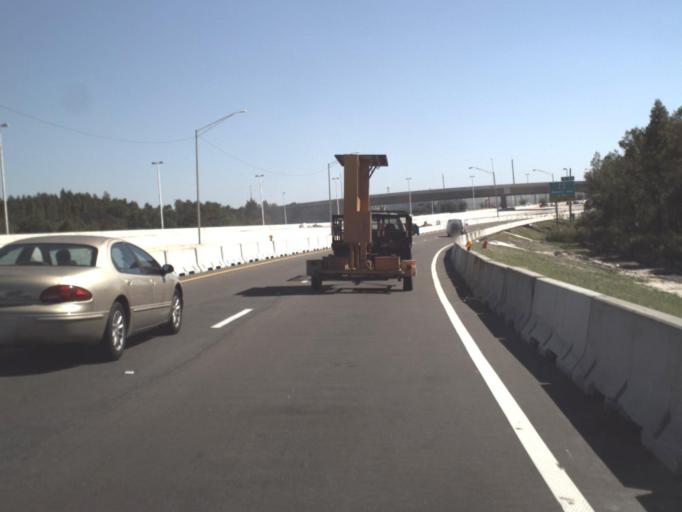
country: US
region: Florida
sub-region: Hillsborough County
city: Town 'n' Country
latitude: 28.0362
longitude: -82.5487
